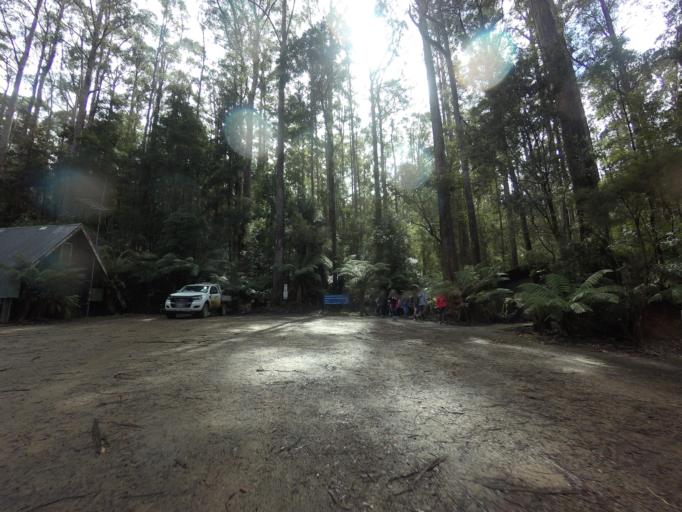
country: AU
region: Tasmania
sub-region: Huon Valley
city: Geeveston
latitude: -43.3826
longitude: 146.8417
